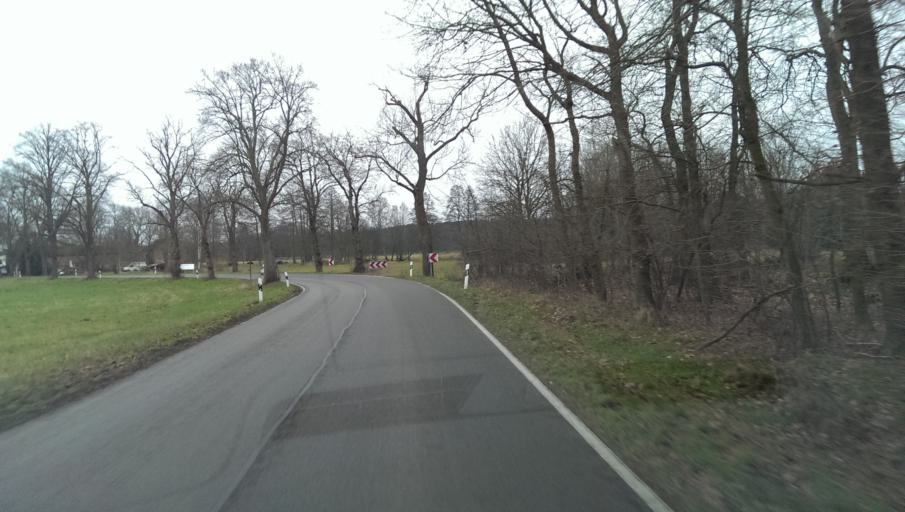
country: DE
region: Brandenburg
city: Mittenwalde
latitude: 52.2162
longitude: 13.5503
